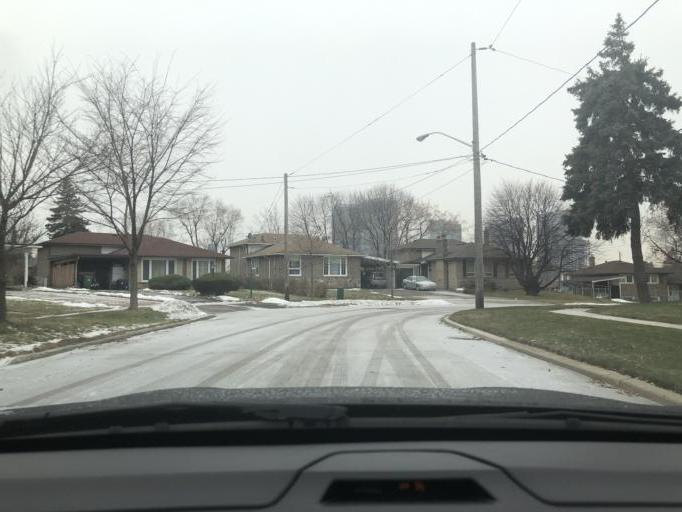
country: CA
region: Ontario
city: Scarborough
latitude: 43.7804
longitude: -79.2724
